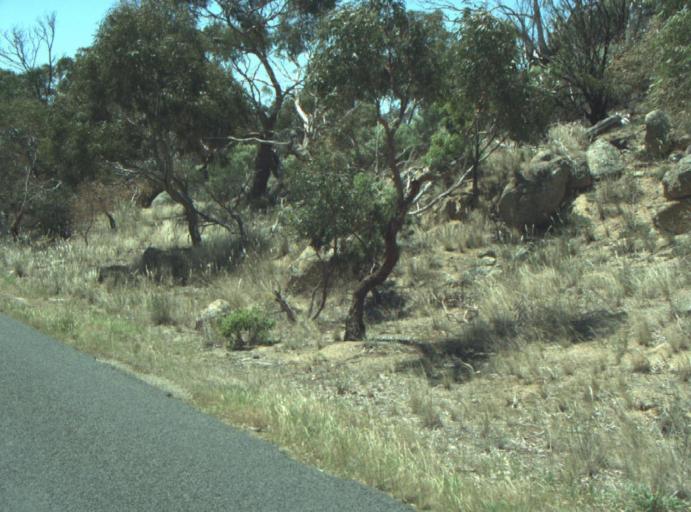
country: AU
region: Victoria
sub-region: Greater Geelong
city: Lara
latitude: -37.8731
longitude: 144.2810
